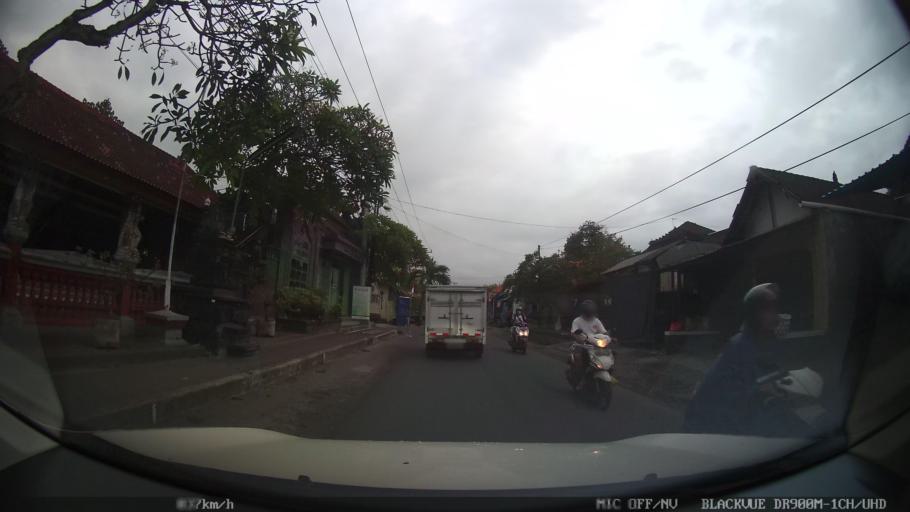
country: ID
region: Bali
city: Banjar Kertajiwa
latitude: -8.6343
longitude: 115.2613
